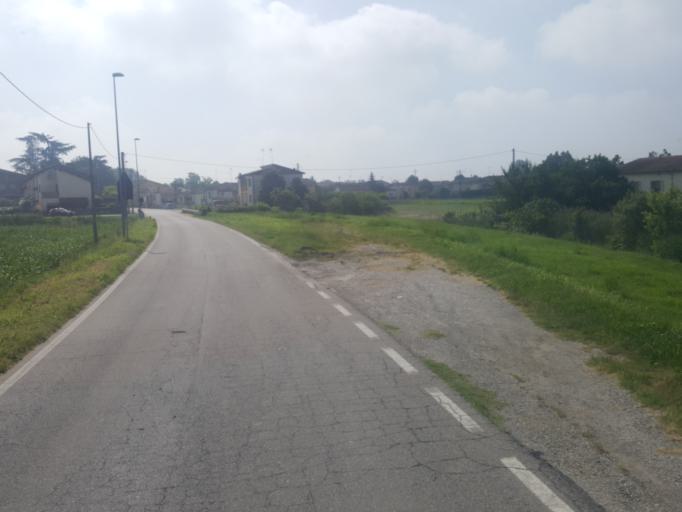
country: IT
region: Veneto
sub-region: Provincia di Rovigo
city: Canaro
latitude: 44.9364
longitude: 11.6709
